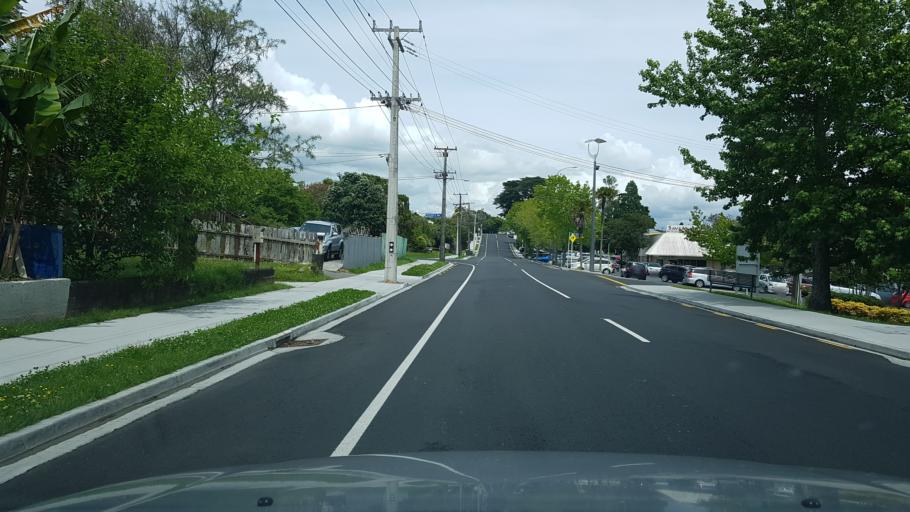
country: NZ
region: Auckland
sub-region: Auckland
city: North Shore
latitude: -36.8011
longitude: 174.7479
